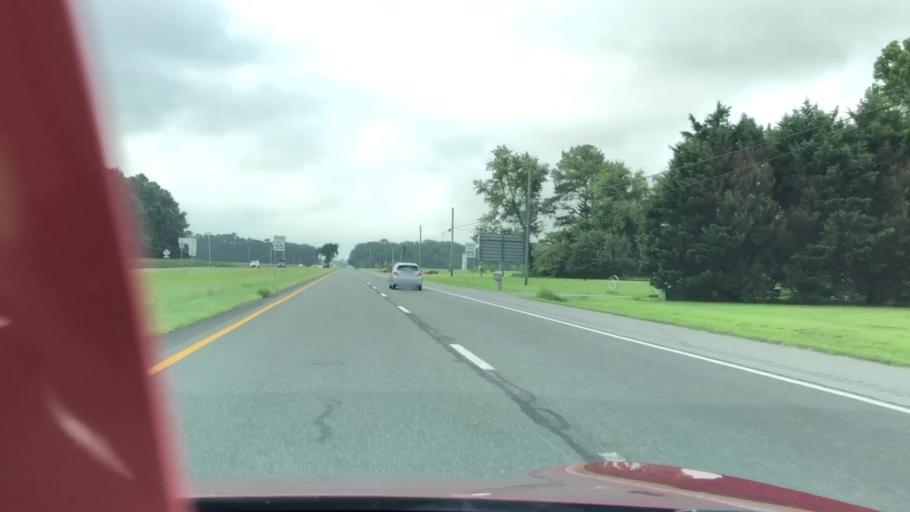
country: US
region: Delaware
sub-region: Kent County
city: Harrington
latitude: 38.8557
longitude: -75.5785
